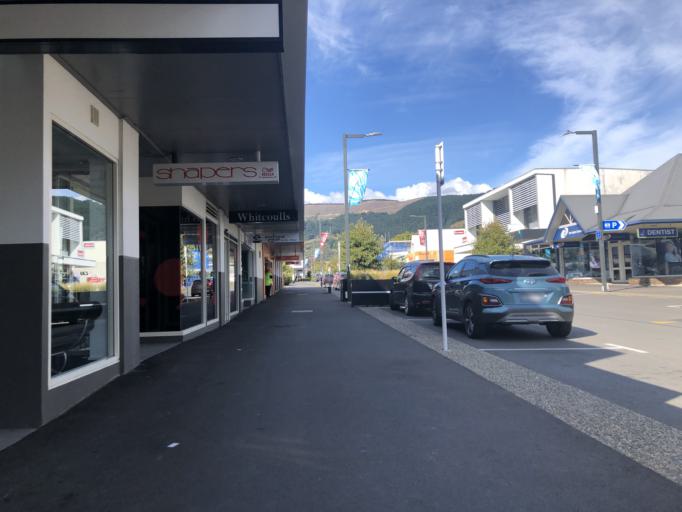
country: NZ
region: Tasman
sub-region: Tasman District
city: Richmond
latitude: -41.3401
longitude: 173.1857
